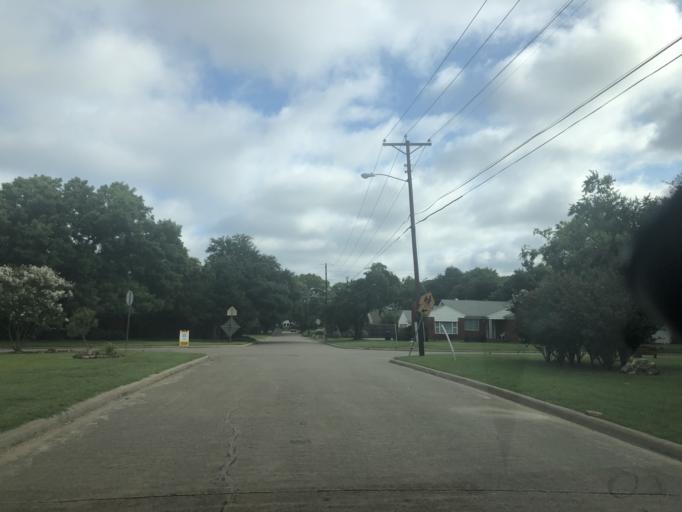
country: US
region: Texas
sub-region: Dallas County
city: University Park
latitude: 32.8706
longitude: -96.8450
